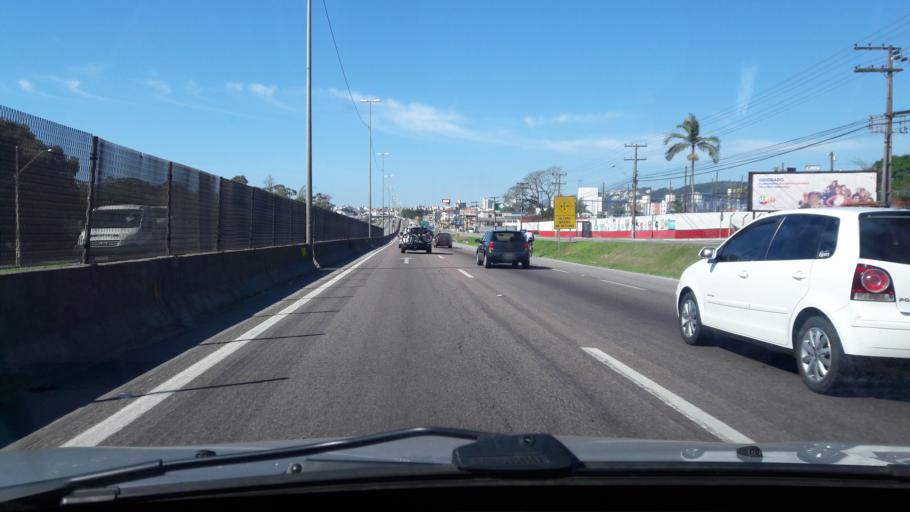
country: BR
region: Santa Catarina
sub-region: Sao Jose
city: Campinas
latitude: -27.5476
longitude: -48.6197
